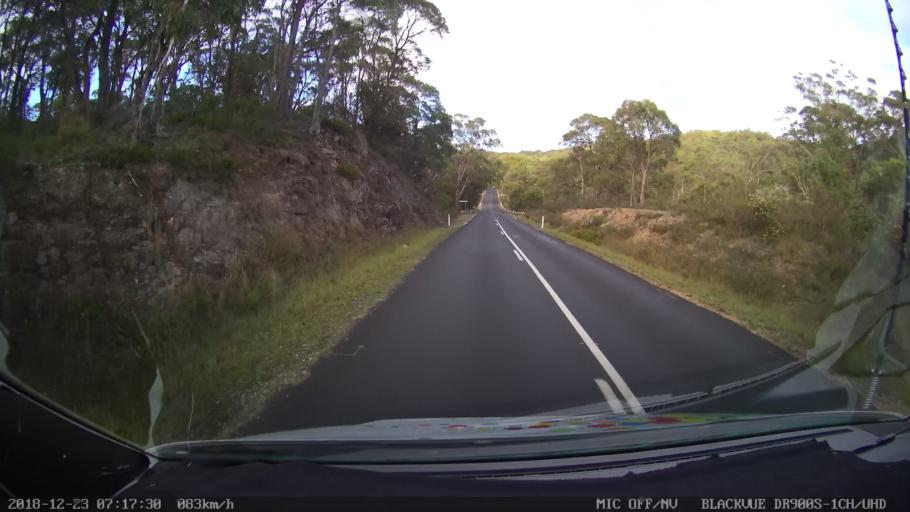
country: AU
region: New South Wales
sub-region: Bellingen
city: Dorrigo
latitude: -30.4677
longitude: 152.3032
